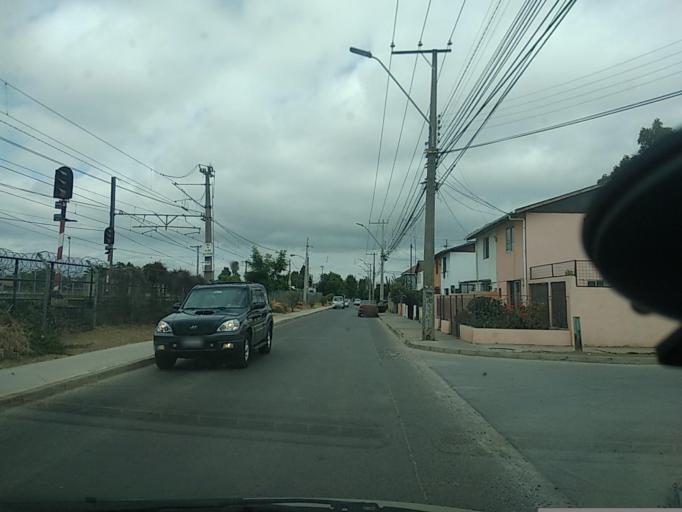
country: CL
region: Valparaiso
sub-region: Provincia de Marga Marga
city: Villa Alemana
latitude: -33.0417
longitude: -71.3636
